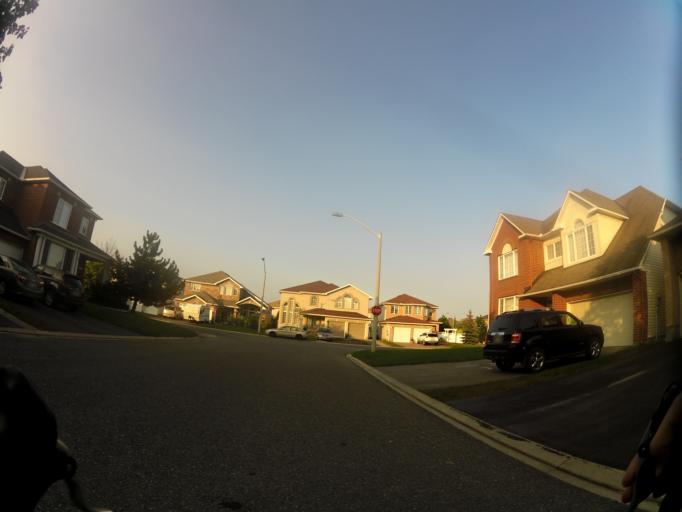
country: CA
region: Ontario
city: Bells Corners
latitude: 45.3528
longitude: -75.9402
